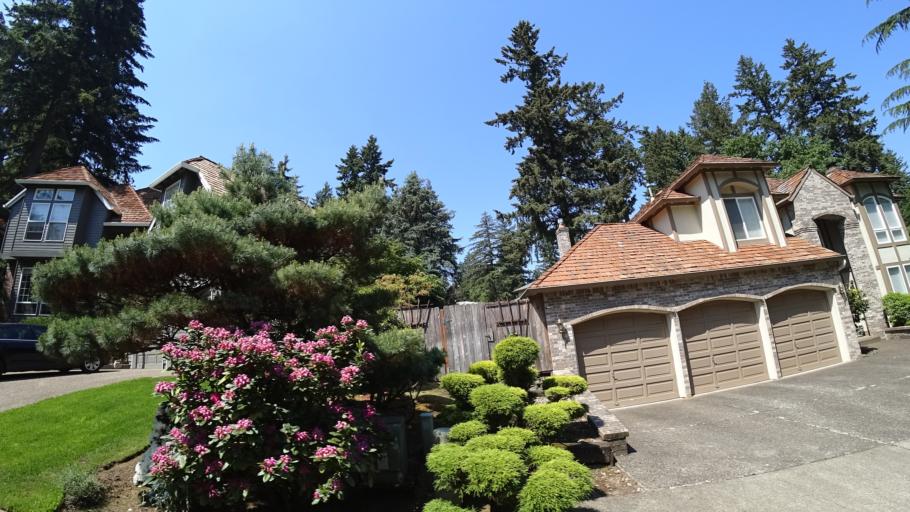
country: US
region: Oregon
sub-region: Clackamas County
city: Lake Oswego
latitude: 45.4414
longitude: -122.7115
